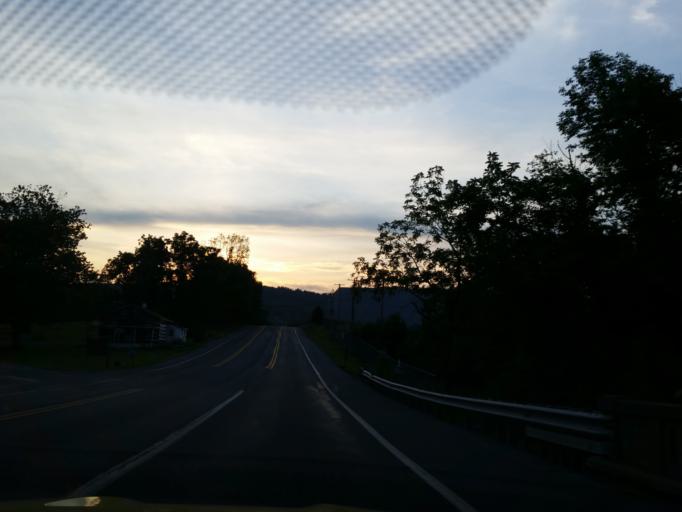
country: US
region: Pennsylvania
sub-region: Lebanon County
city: Jonestown
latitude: 40.4238
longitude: -76.5810
